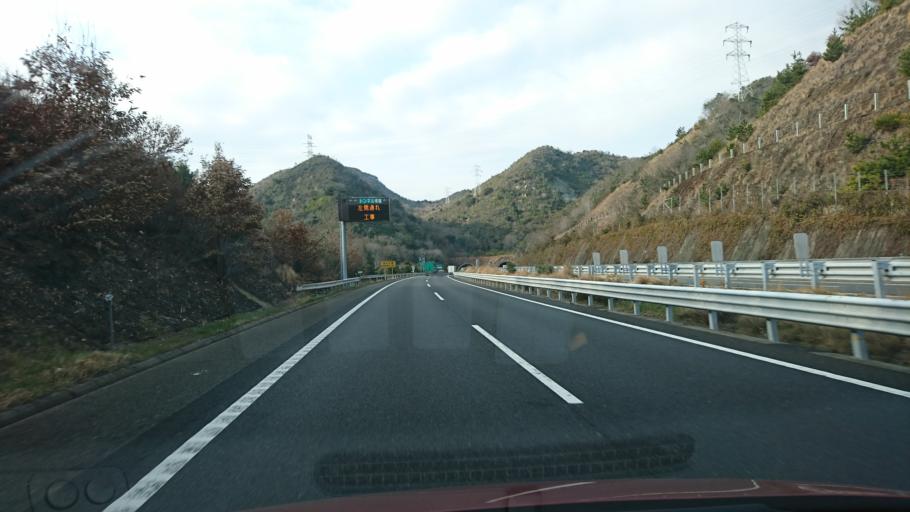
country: JP
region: Hyogo
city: Aioi
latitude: 34.7949
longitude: 134.4315
